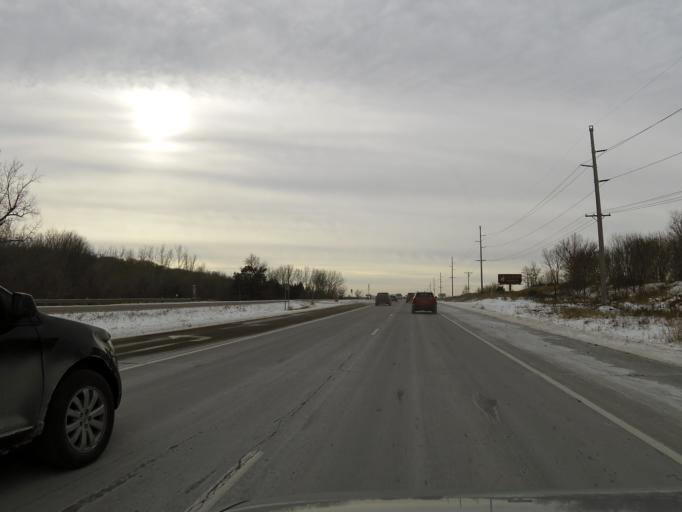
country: US
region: Minnesota
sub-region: Carver County
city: Carver
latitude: 44.7503
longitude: -93.5868
